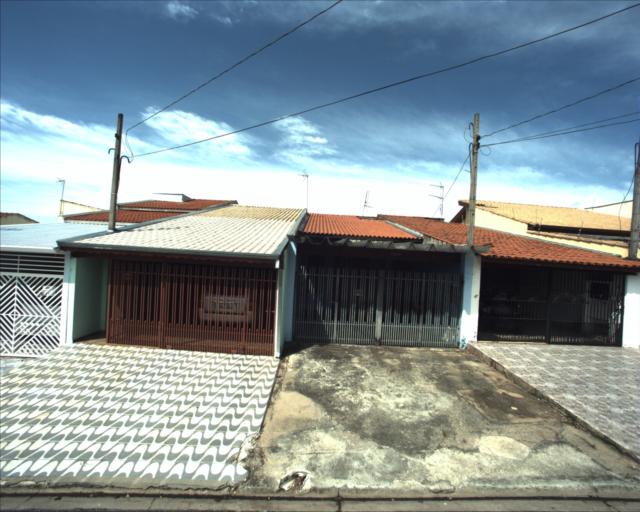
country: BR
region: Sao Paulo
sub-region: Sorocaba
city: Sorocaba
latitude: -23.5186
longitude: -47.5057
